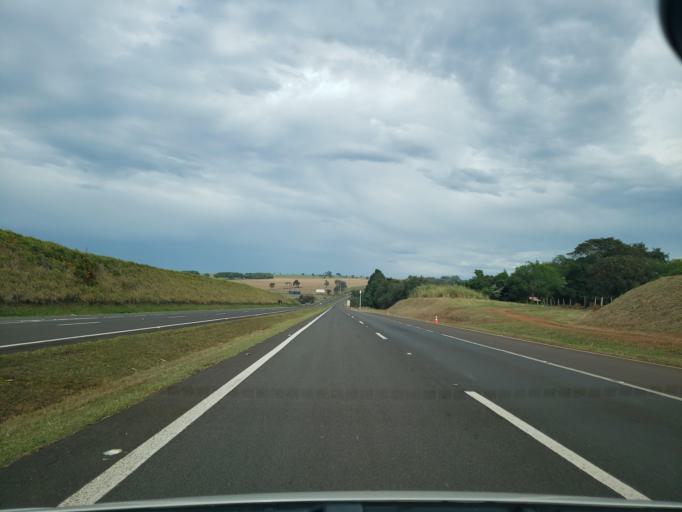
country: BR
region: Sao Paulo
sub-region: Dois Corregos
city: Dois Corregos
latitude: -22.2512
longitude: -48.3608
